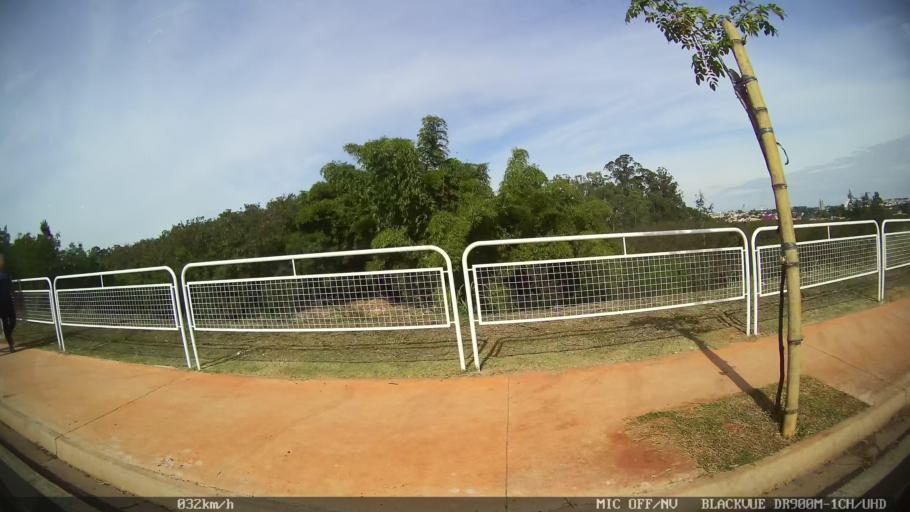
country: BR
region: Sao Paulo
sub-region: Piracicaba
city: Piracicaba
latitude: -22.7498
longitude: -47.6179
